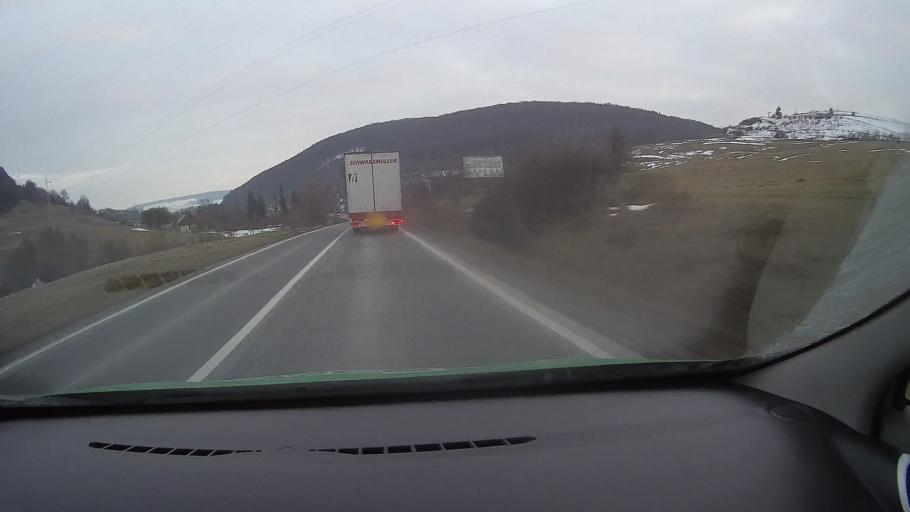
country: RO
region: Harghita
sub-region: Municipiul Odorheiu Secuiesc
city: Odorheiu Secuiesc
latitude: 46.3379
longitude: 25.2699
